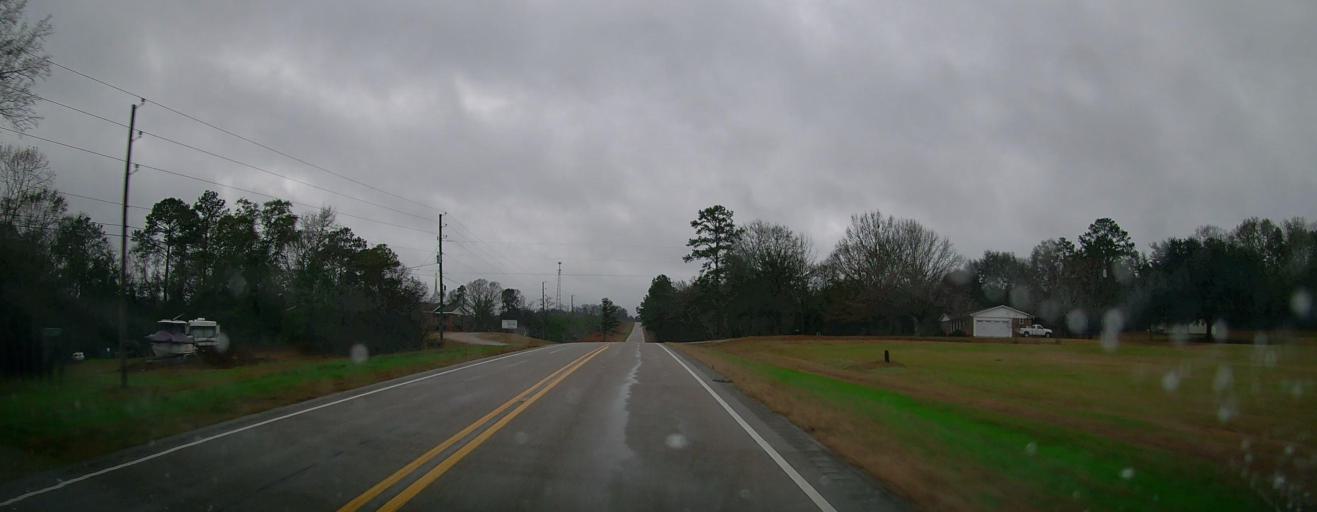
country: US
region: Alabama
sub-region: Autauga County
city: Pine Level
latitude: 32.5372
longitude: -86.6410
